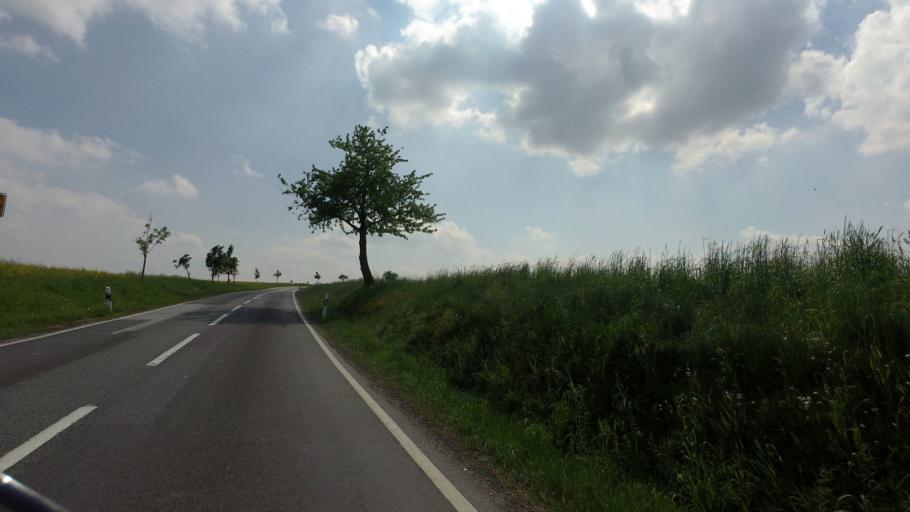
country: DE
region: Saxony
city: Weissenberg
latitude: 51.2199
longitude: 14.6688
